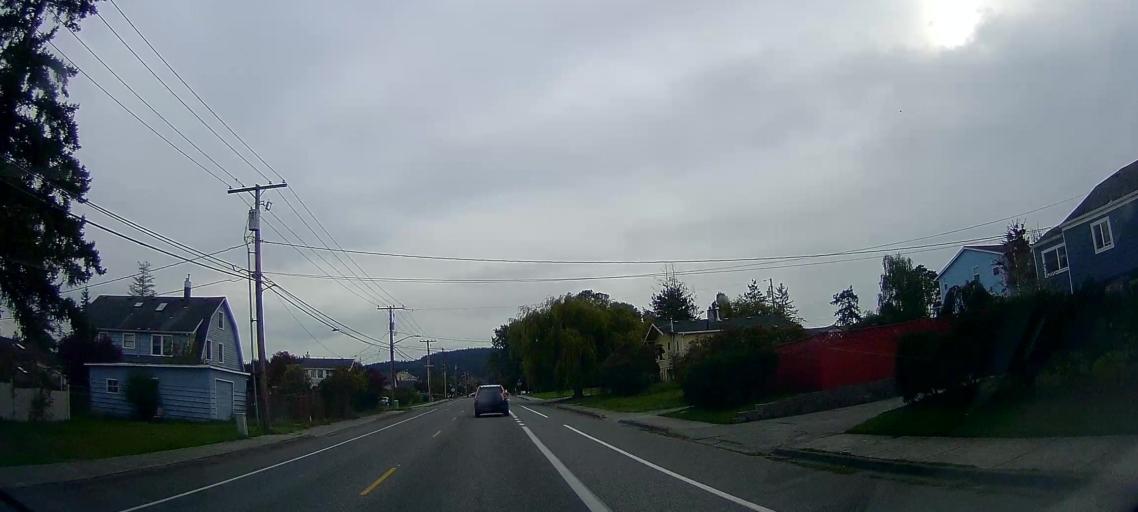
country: US
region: Washington
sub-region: Skagit County
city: Anacortes
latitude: 48.4979
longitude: -122.6176
